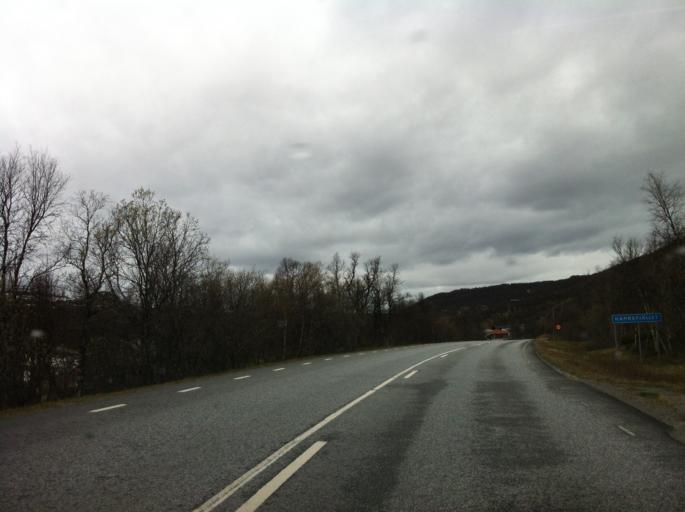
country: NO
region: Sor-Trondelag
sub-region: Tydal
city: Aas
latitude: 62.5706
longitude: 12.2350
